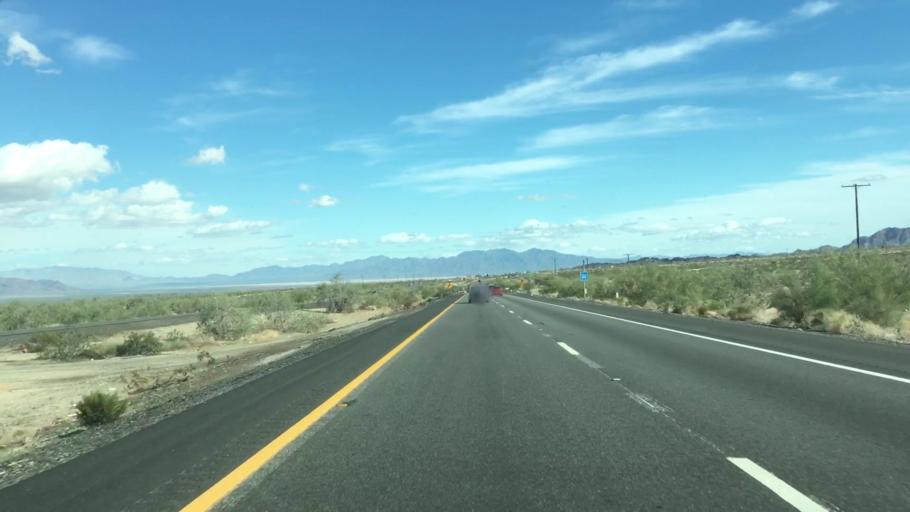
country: US
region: California
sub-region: Imperial County
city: Niland
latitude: 33.6985
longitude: -115.4702
